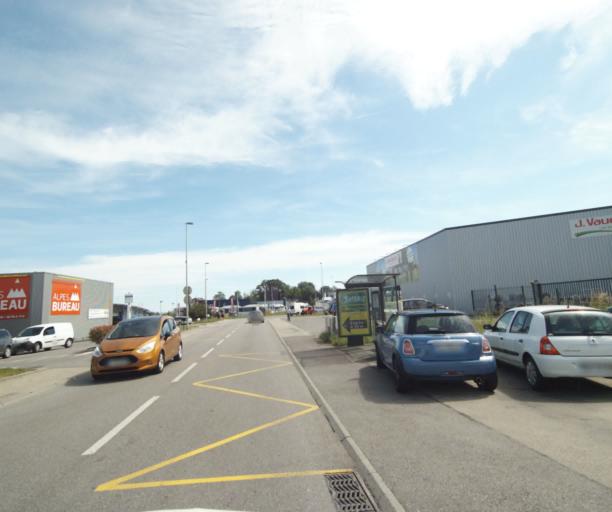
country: FR
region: Rhone-Alpes
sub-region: Departement de la Haute-Savoie
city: Anthy-sur-Leman
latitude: 46.3494
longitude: 6.4401
